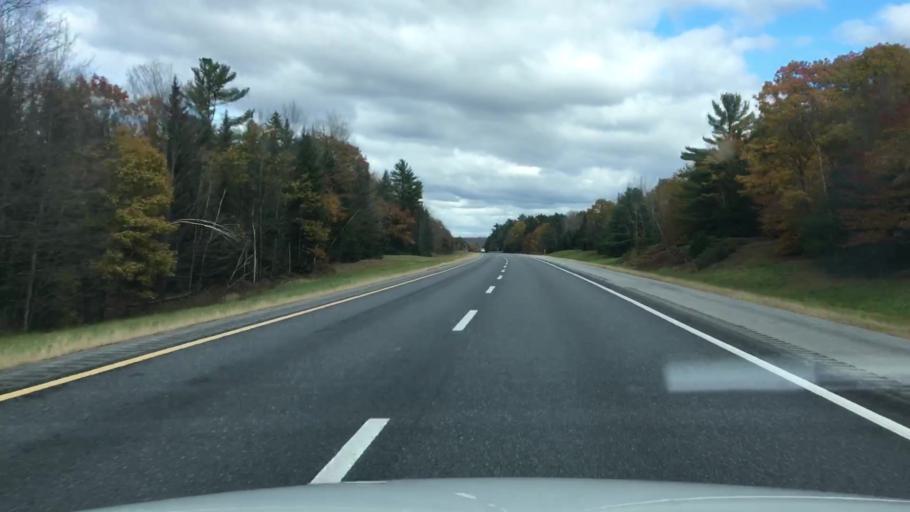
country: US
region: Maine
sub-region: Sagadahoc County
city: Richmond
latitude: 44.0487
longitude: -69.8913
